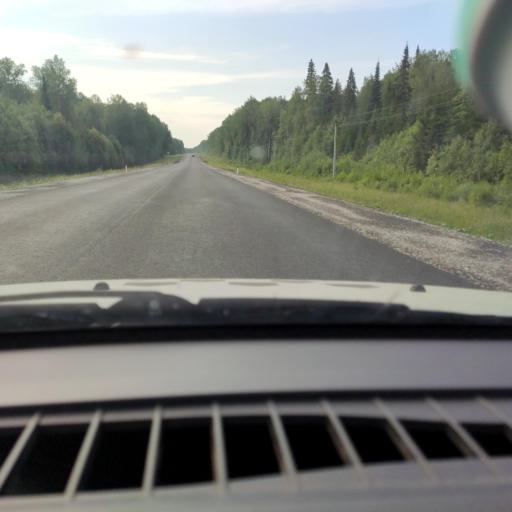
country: RU
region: Perm
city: Siva
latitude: 58.5729
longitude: 53.8873
